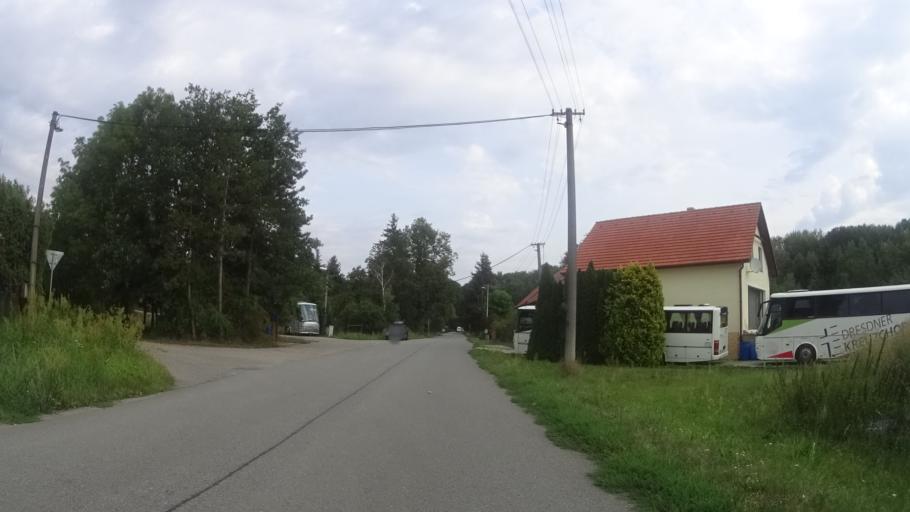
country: CZ
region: Zlin
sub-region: Okres Kromeriz
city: Kromeriz
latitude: 49.3249
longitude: 17.3878
